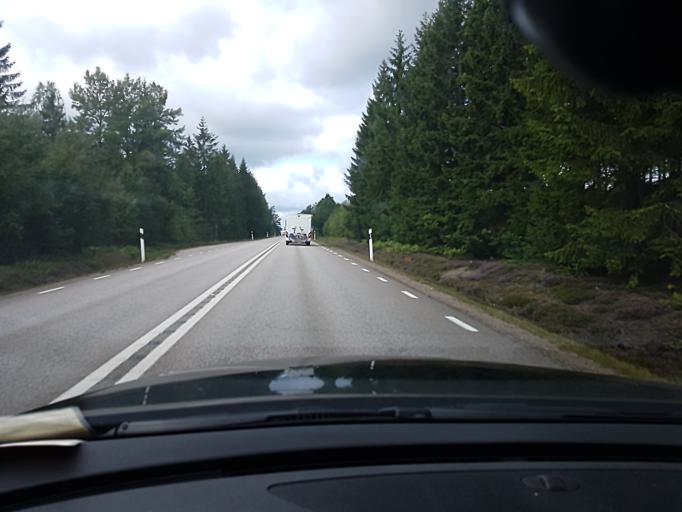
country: SE
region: Kronoberg
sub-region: Lessebo Kommun
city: Lessebo
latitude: 56.7298
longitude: 15.3564
